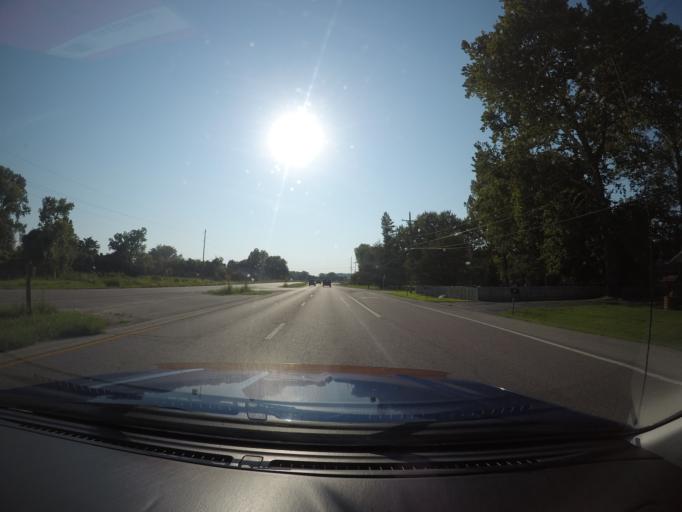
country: US
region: Kansas
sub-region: Wyandotte County
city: Edwardsville
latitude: 39.0638
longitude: -94.8367
